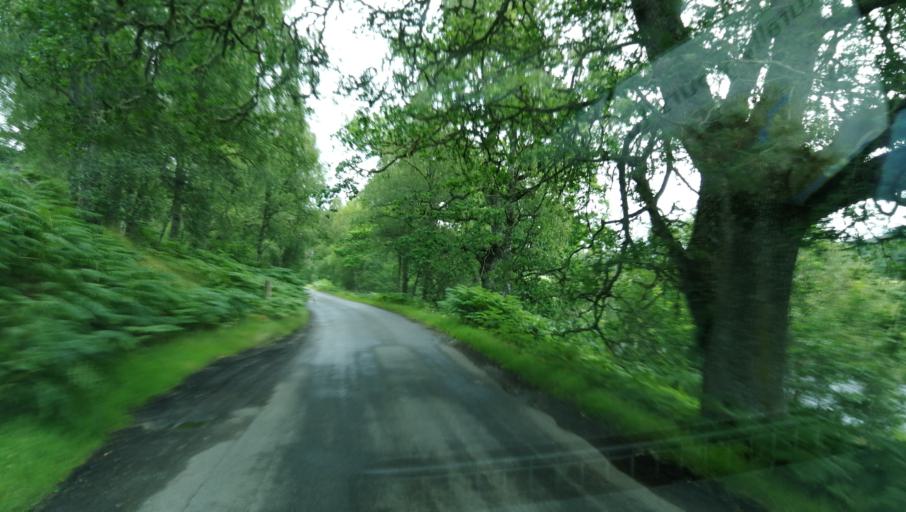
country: GB
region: Scotland
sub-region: Highland
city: Beauly
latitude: 57.3271
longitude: -4.7937
